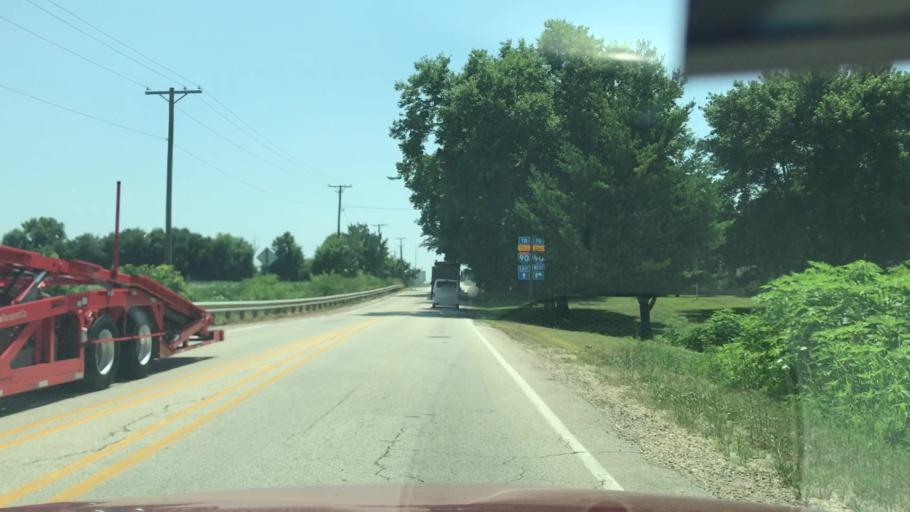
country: US
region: Illinois
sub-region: Winnebago County
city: Cherry Valley
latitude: 42.2382
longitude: -88.9007
